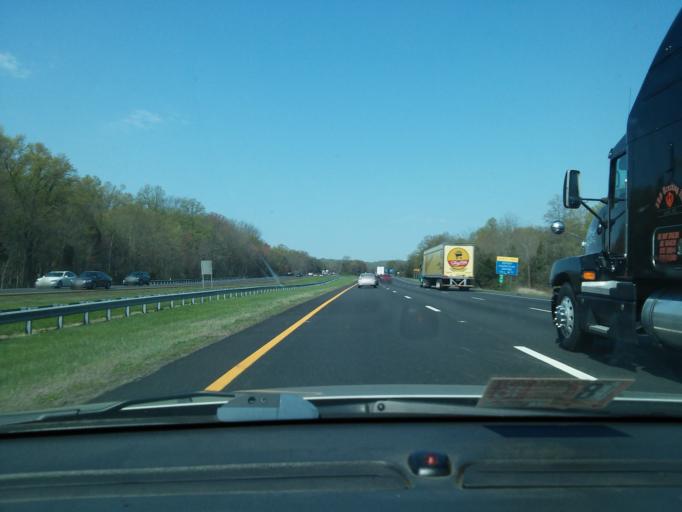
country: US
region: New Jersey
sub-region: Somerset County
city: Martinsville
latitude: 40.6464
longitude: -74.5476
